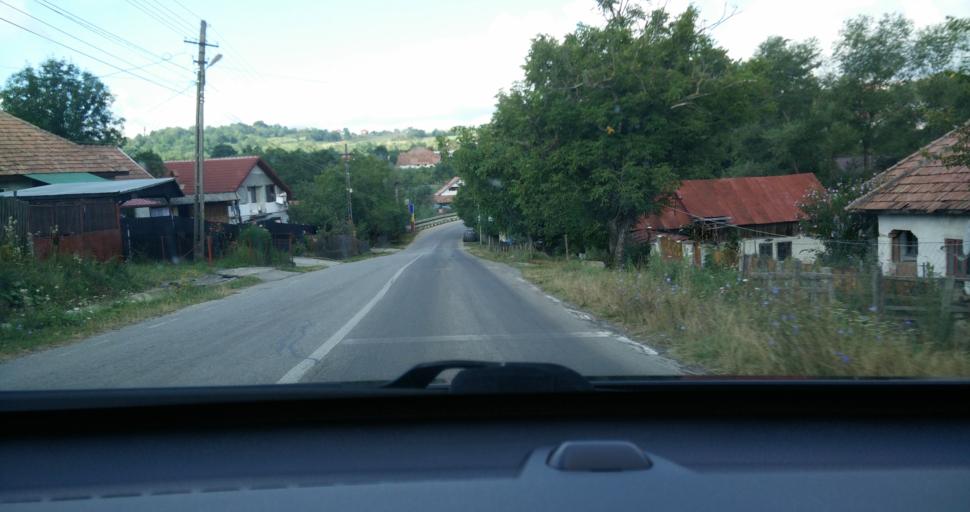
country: RO
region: Gorj
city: Novaci-Straini
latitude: 45.1761
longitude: 23.7084
